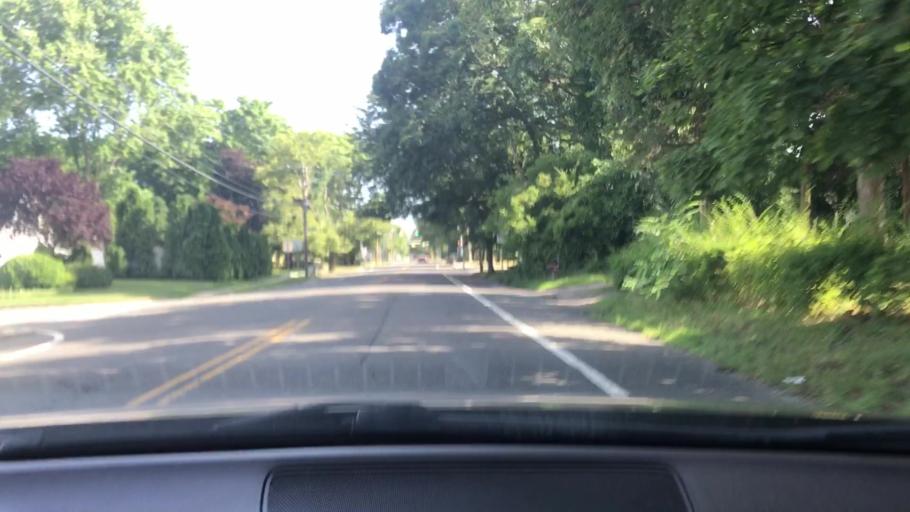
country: US
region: New York
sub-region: Suffolk County
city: Holbrook
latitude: 40.8248
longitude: -73.0805
